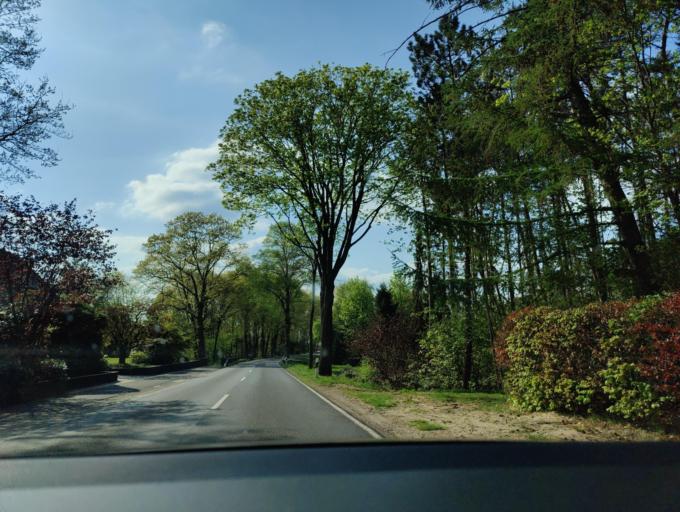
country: DE
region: Lower Saxony
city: Engden
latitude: 52.3903
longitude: 7.1623
